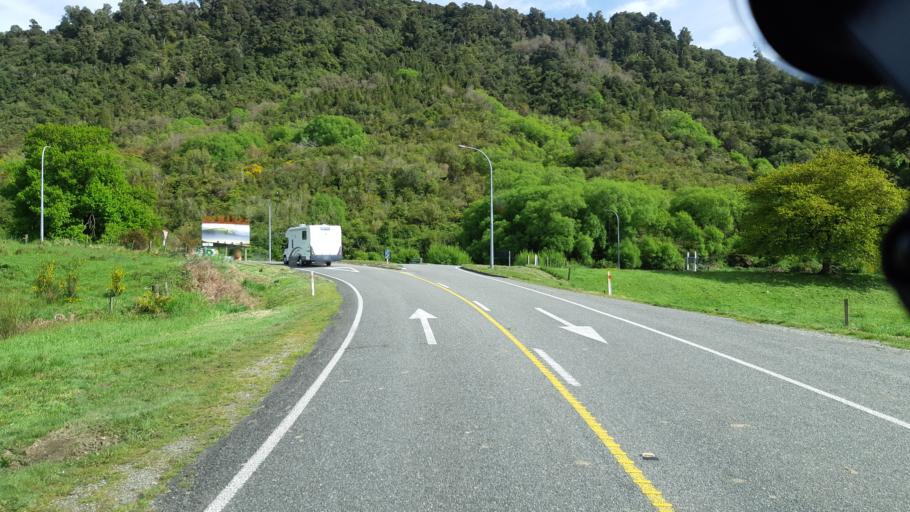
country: NZ
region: West Coast
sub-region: Buller District
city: Westport
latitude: -41.8583
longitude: 171.9379
